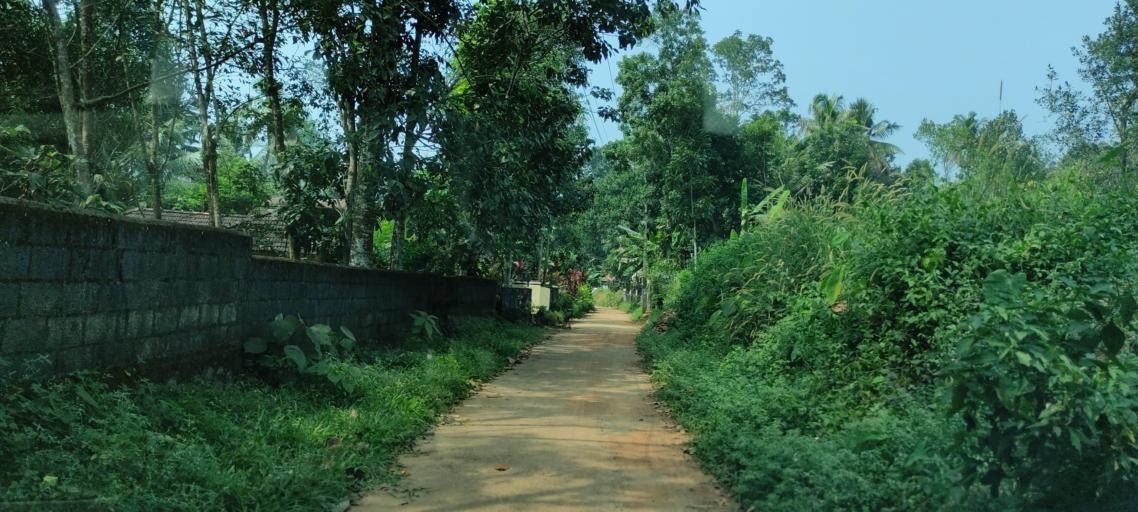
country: IN
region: Kerala
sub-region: Pattanamtitta
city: Adur
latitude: 9.2031
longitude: 76.6937
